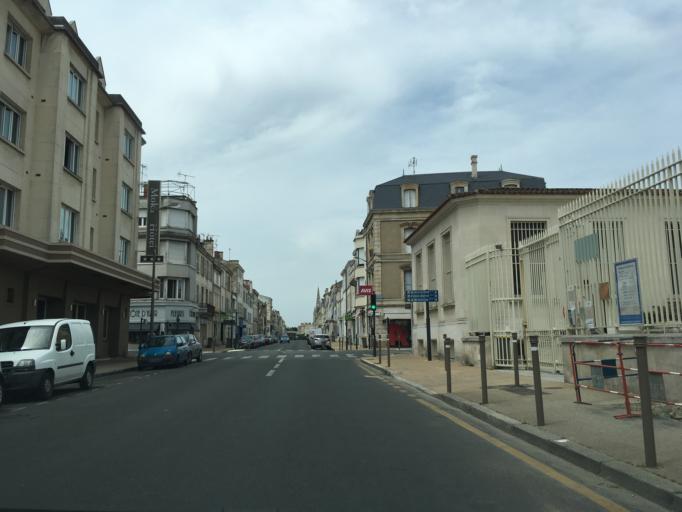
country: FR
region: Poitou-Charentes
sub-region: Departement des Deux-Sevres
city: Niort
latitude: 46.3199
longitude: -0.4563
